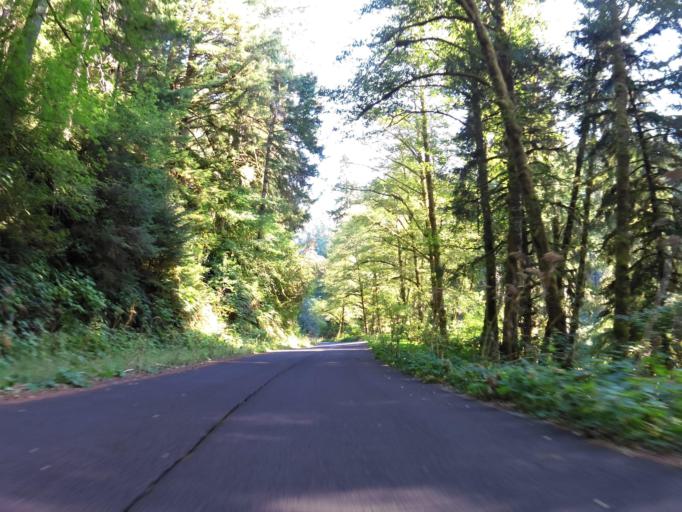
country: US
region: Oregon
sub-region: Lincoln County
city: Rose Lodge
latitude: 45.0370
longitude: -123.9122
